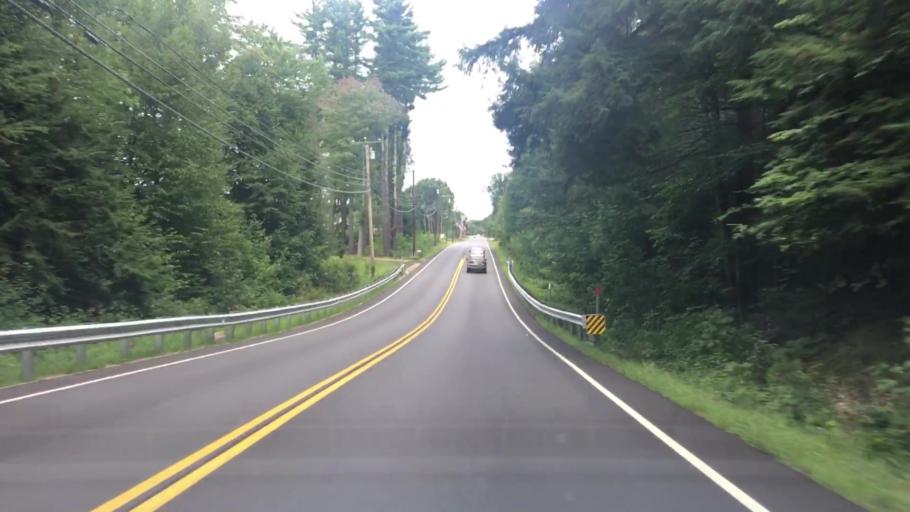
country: US
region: Maine
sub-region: York County
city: Dayton
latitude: 43.5005
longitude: -70.5883
